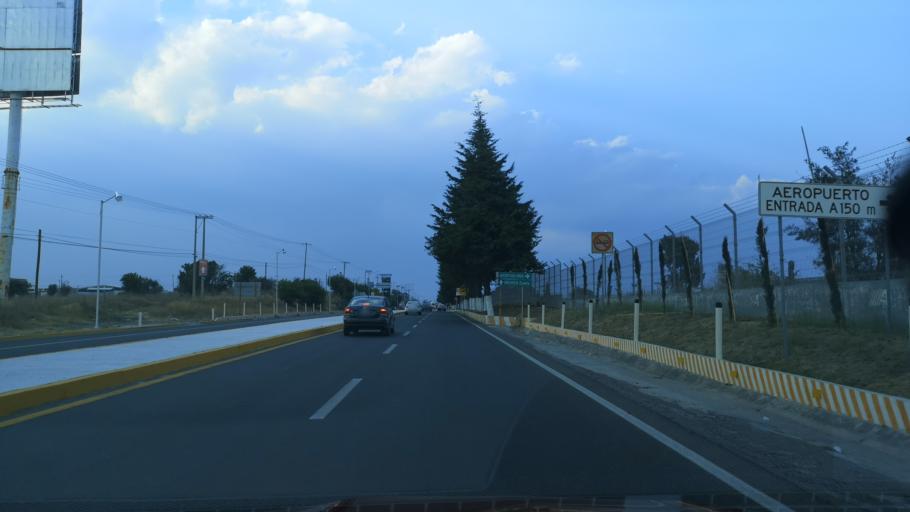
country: MX
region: Puebla
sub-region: Huejotzingo
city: Los Encinos
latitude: 19.1616
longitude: -98.3773
